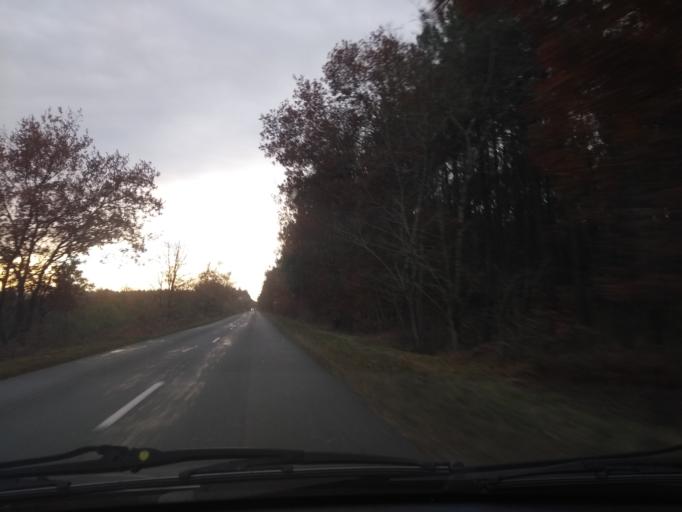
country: FR
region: Aquitaine
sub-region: Departement de la Gironde
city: Saucats
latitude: 44.6465
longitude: -0.6195
